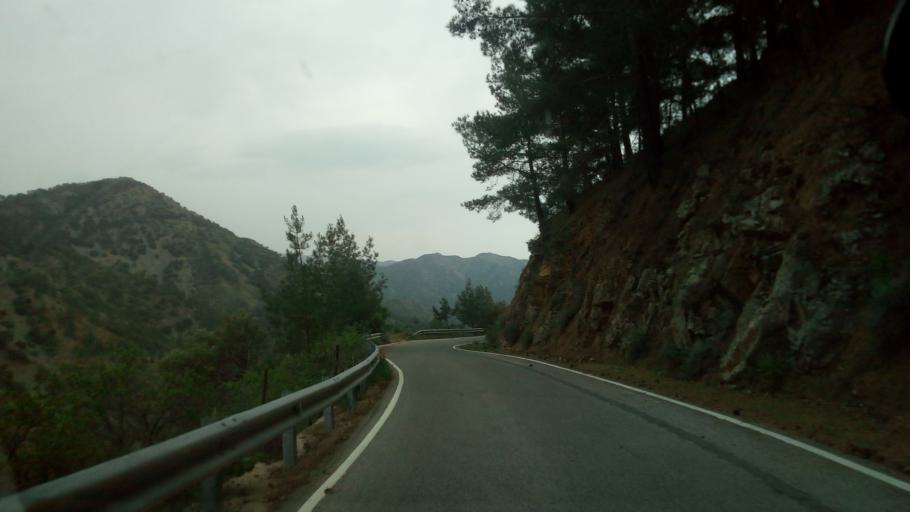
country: CY
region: Lefkosia
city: Kakopetria
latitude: 34.9650
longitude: 32.7491
